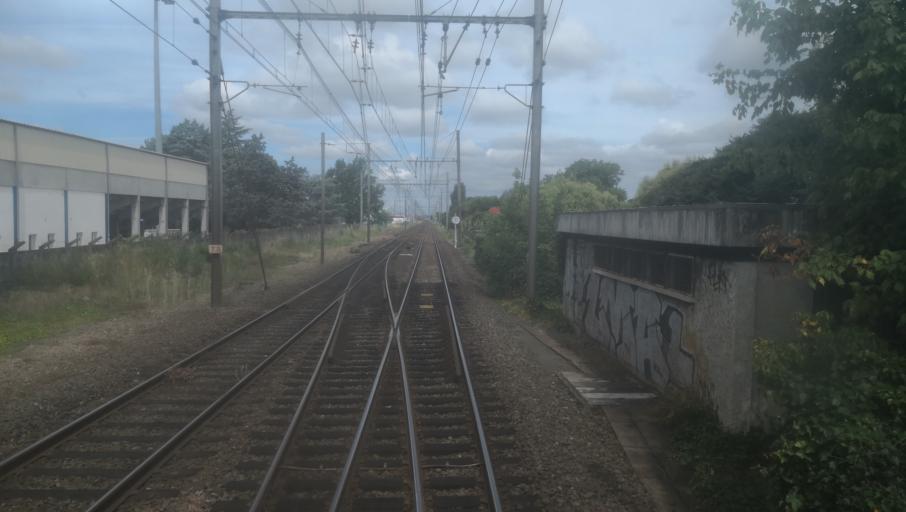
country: FR
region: Aquitaine
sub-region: Departement du Lot-et-Garonne
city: Marmande
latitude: 44.5076
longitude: 0.1594
